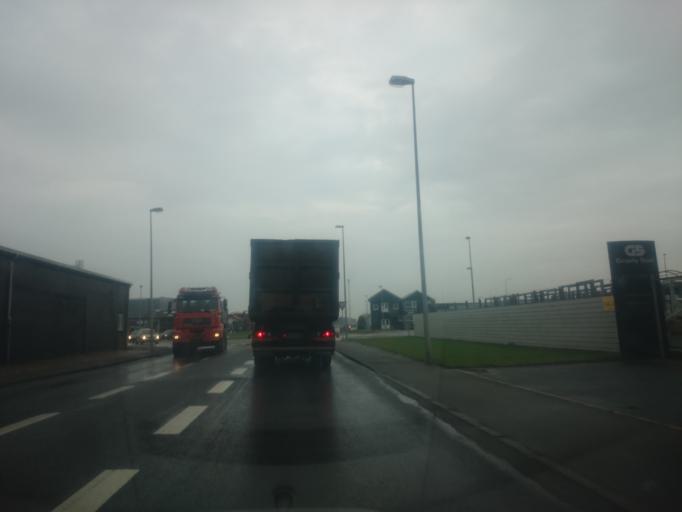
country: DK
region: South Denmark
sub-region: Esbjerg Kommune
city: Esbjerg
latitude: 55.4718
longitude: 8.4318
